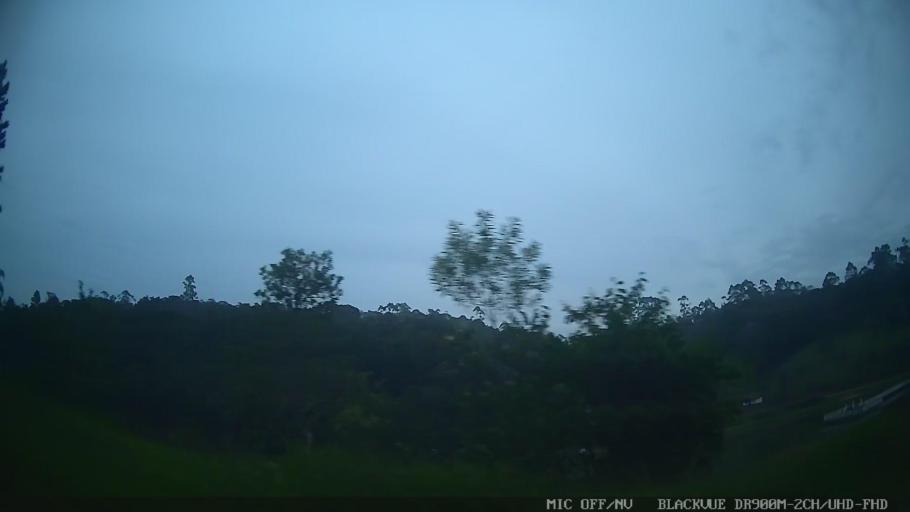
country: BR
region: Sao Paulo
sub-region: Rio Grande Da Serra
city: Rio Grande da Serra
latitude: -23.6961
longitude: -46.3073
